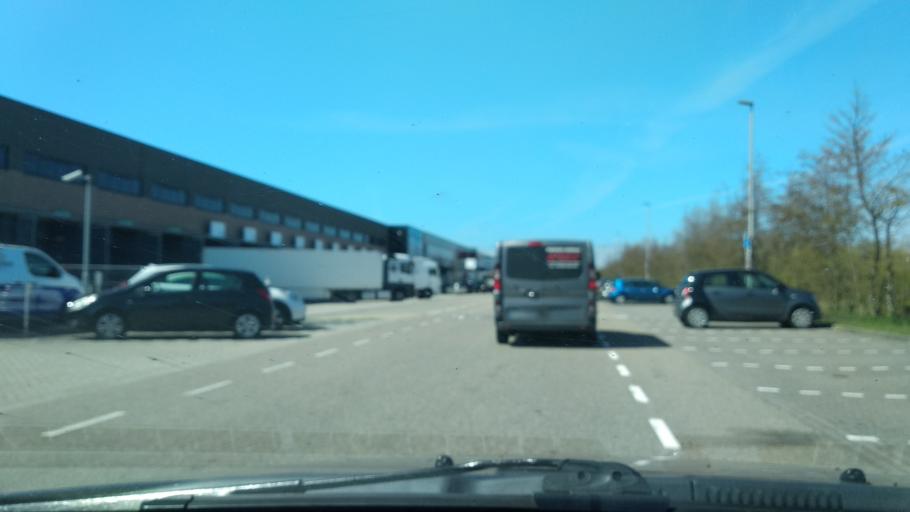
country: NL
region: South Holland
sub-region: Gemeente Westland
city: Honselersdijk
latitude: 51.9975
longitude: 4.2370
